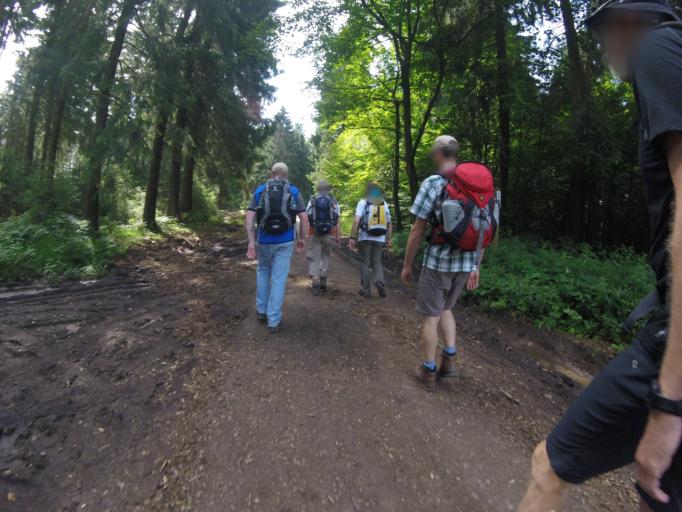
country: DE
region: Hesse
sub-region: Regierungsbezirk Giessen
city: Ulrichstein
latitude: 50.5292
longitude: 9.2422
